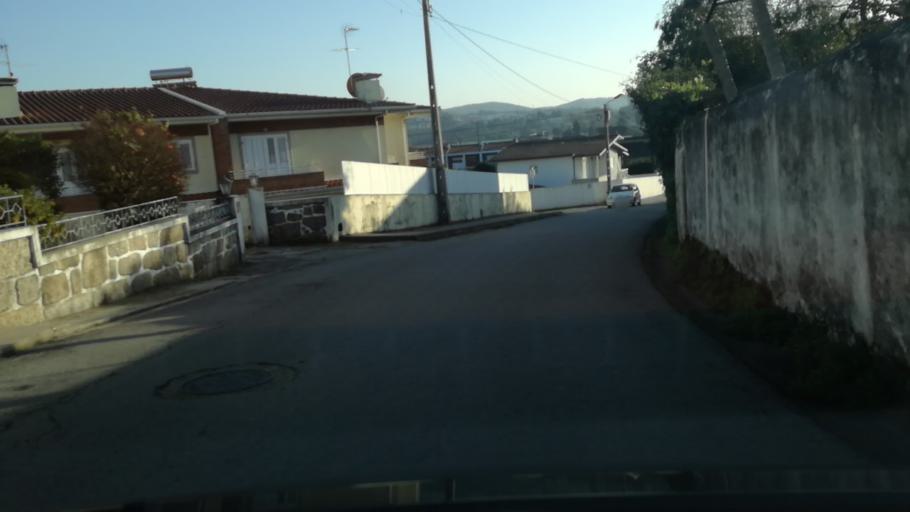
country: PT
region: Braga
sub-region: Vila Nova de Famalicao
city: Ferreiros
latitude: 41.3538
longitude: -8.5290
